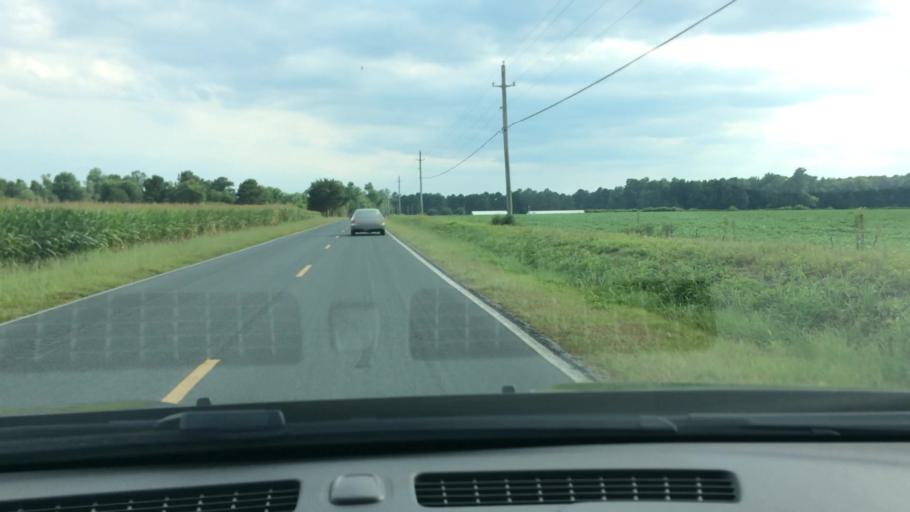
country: US
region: North Carolina
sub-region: Pitt County
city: Ayden
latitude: 35.4697
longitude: -77.3858
